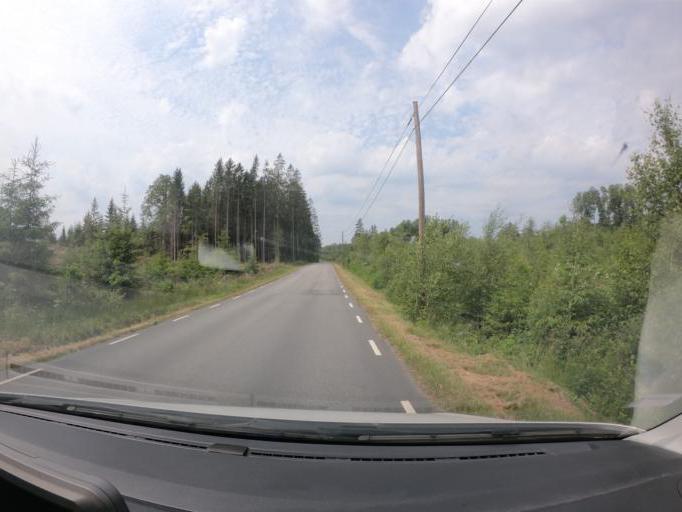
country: SE
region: Skane
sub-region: Hassleholms Kommun
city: Bjarnum
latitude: 56.2854
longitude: 13.6800
